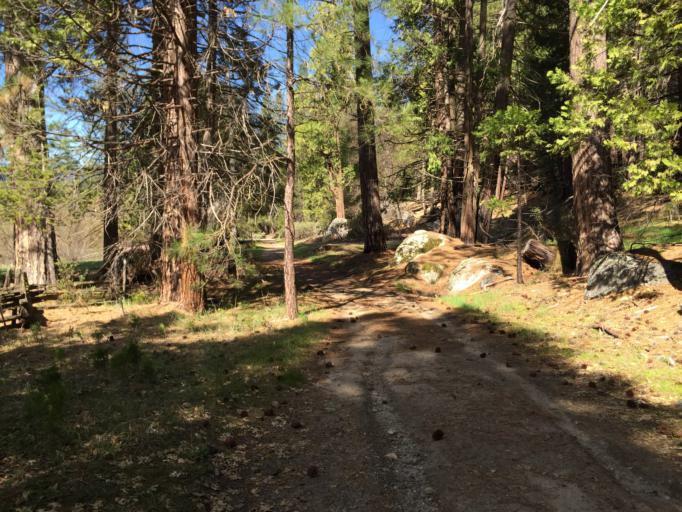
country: US
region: California
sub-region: Madera County
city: Ahwahnee
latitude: 37.5318
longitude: -119.6438
